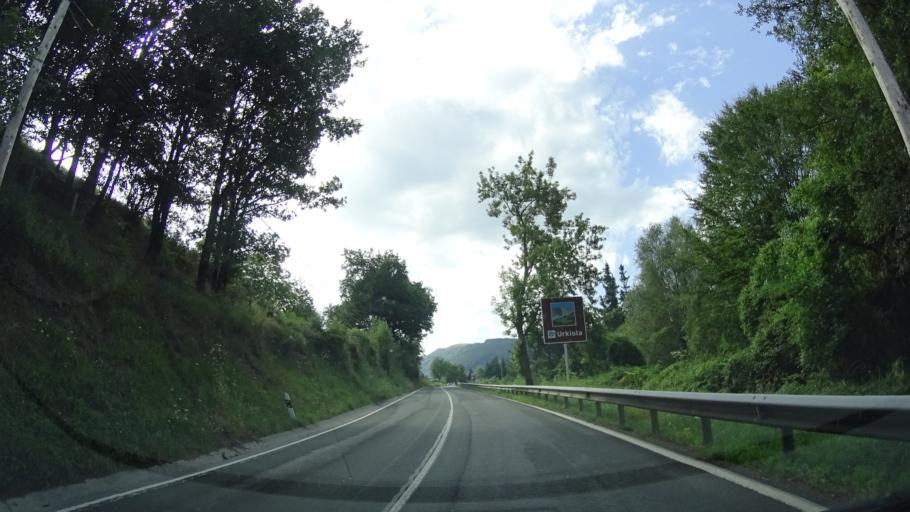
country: ES
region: Basque Country
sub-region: Bizkaia
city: Manaria
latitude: 43.1130
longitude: -2.6459
